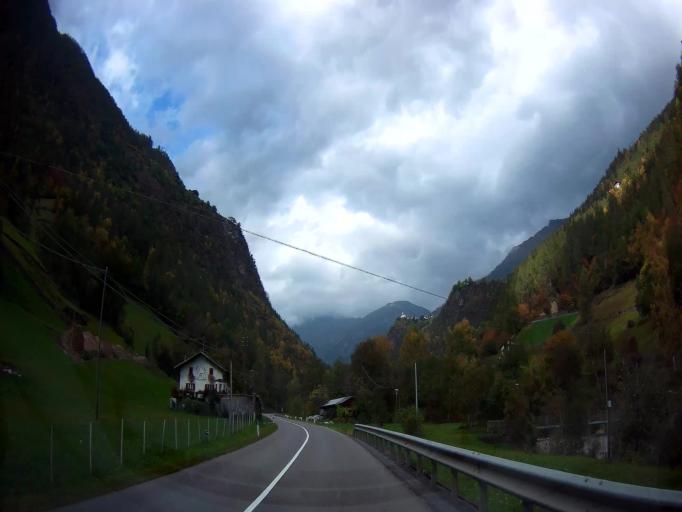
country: IT
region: Trentino-Alto Adige
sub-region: Bolzano
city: Certosa
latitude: 46.6744
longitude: 10.9403
